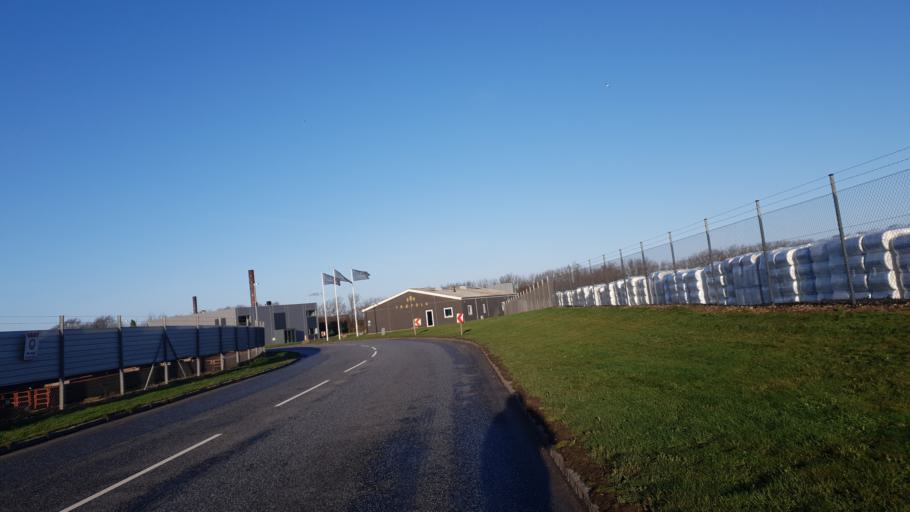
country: DK
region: Central Jutland
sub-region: Hedensted Kommune
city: Hedensted
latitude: 55.7960
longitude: 9.6781
